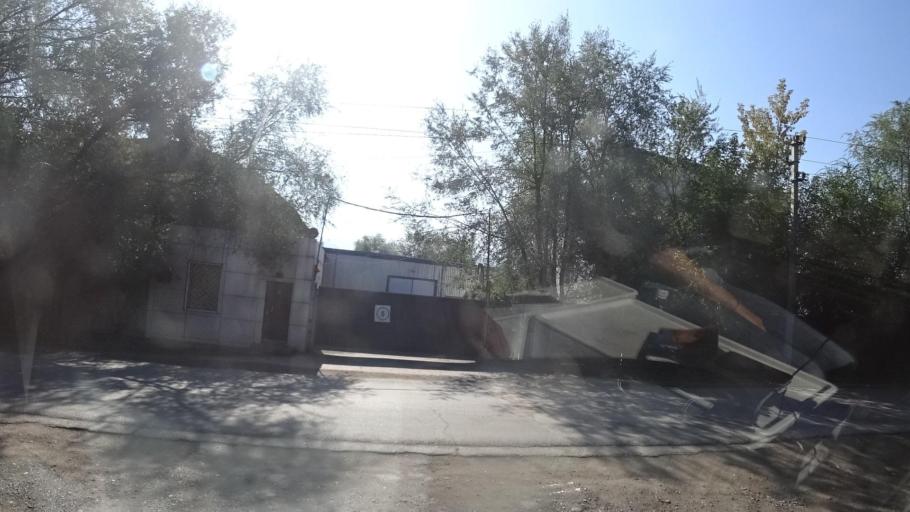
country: KZ
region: Almaty Oblysy
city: Pervomayskiy
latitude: 43.3301
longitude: 77.0000
